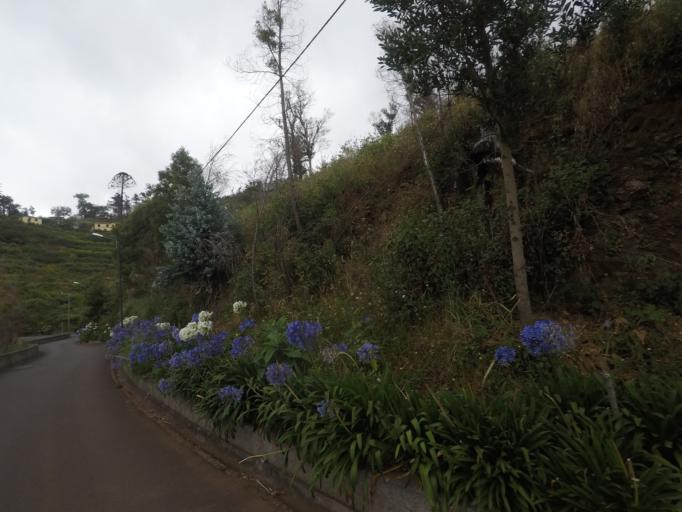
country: PT
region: Madeira
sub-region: Funchal
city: Nossa Senhora do Monte
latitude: 32.6674
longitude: -16.8876
